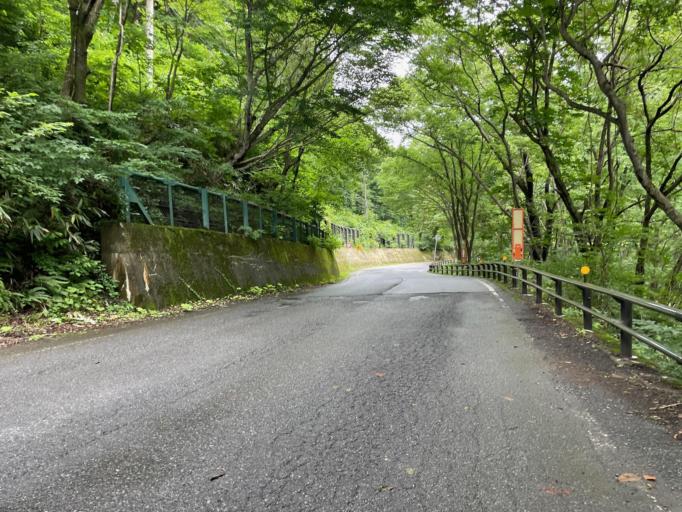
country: JP
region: Gunma
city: Numata
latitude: 36.8262
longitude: 138.9714
